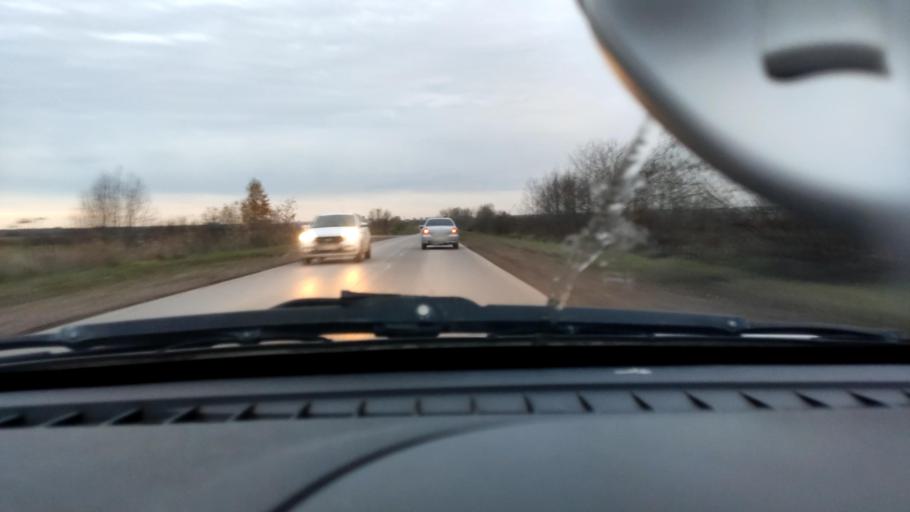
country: RU
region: Perm
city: Kondratovo
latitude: 57.9900
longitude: 56.0950
